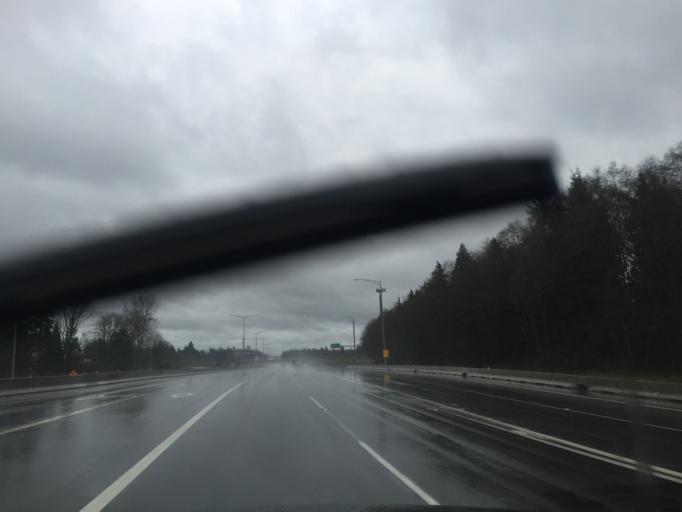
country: CA
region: British Columbia
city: Coquitlam
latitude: 49.1942
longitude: -122.7860
